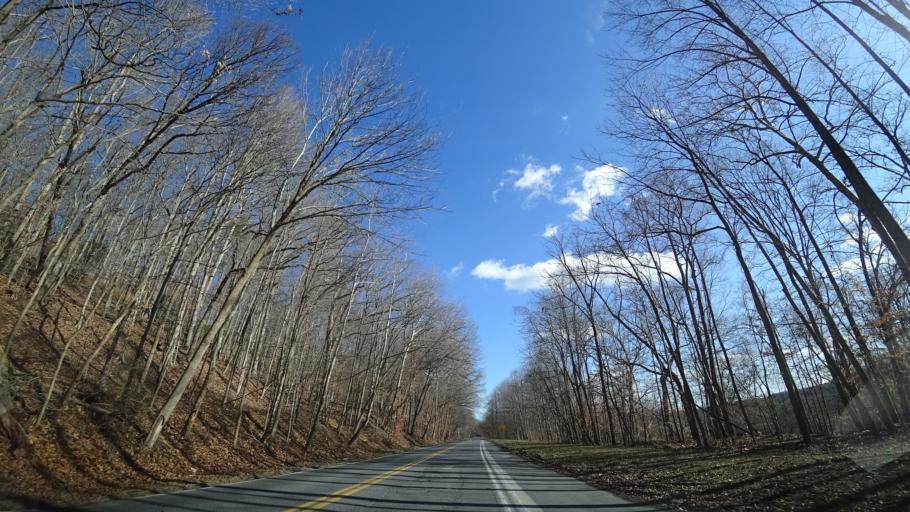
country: US
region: Maryland
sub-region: Montgomery County
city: Potomac
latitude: 38.9792
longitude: -77.2114
